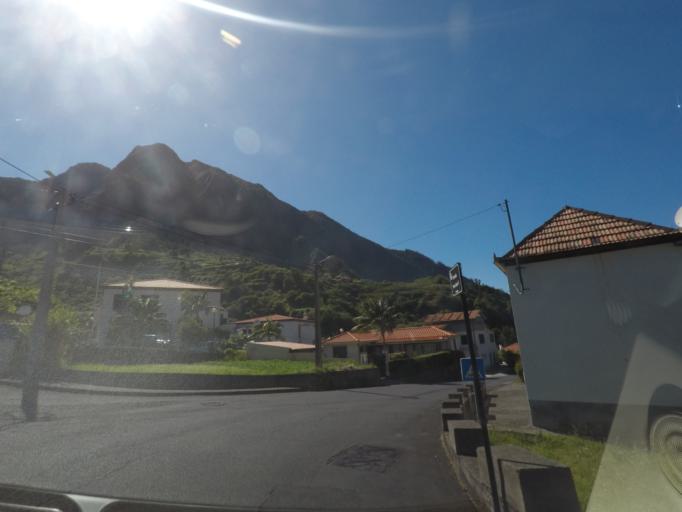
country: PT
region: Madeira
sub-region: Sao Vicente
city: Sao Vicente
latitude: 32.7933
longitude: -17.0425
